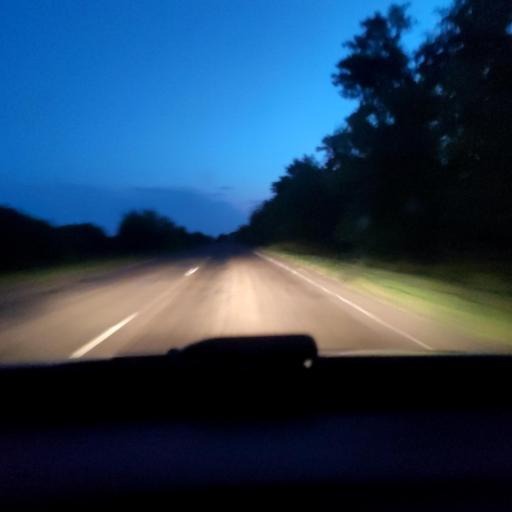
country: RU
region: Voronezj
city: Panino
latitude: 51.6349
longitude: 40.0876
